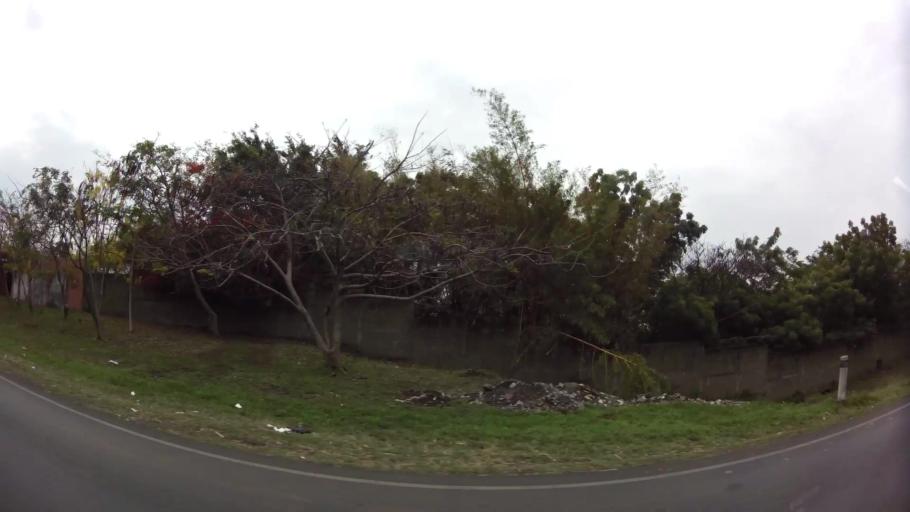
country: NI
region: Masaya
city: Masaya
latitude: 11.9607
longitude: -86.0841
